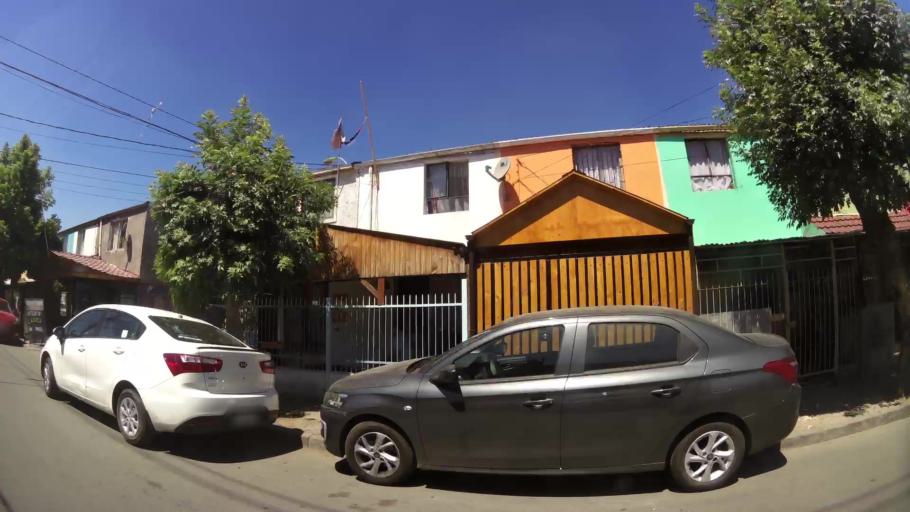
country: CL
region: Santiago Metropolitan
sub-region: Provincia de Maipo
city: San Bernardo
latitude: -33.5833
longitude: -70.6704
